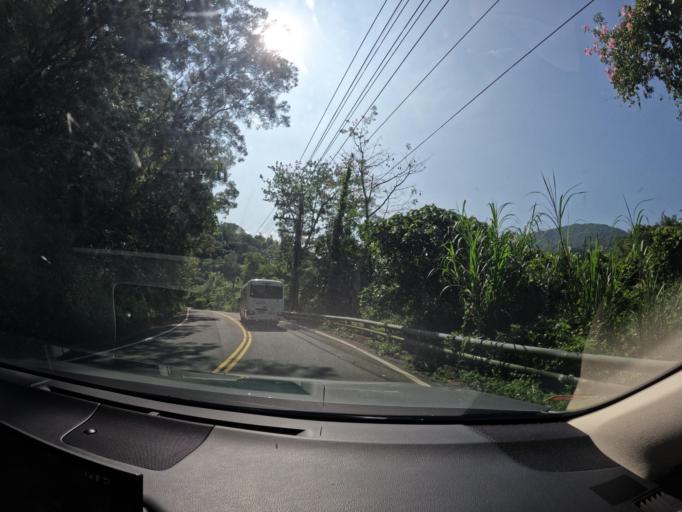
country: TW
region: Taiwan
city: Yujing
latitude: 23.0719
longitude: 120.6449
